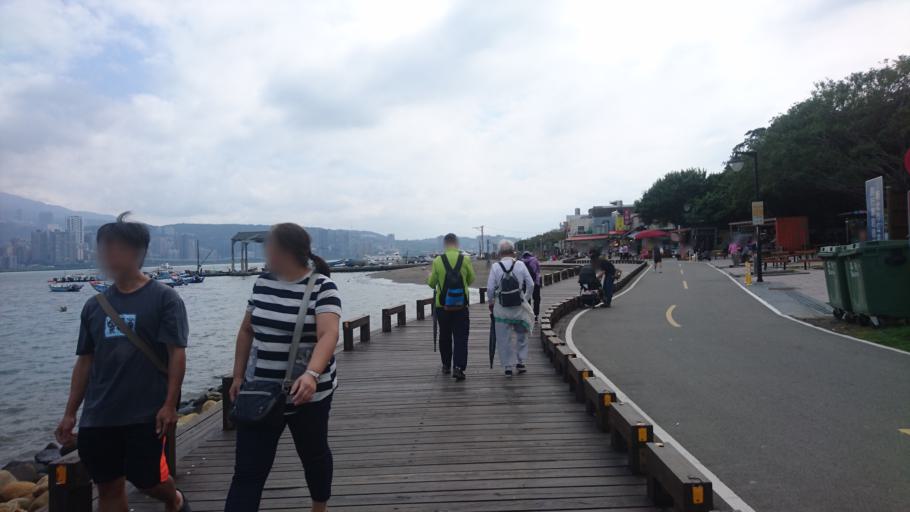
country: TW
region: Taipei
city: Taipei
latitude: 25.1603
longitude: 121.4334
